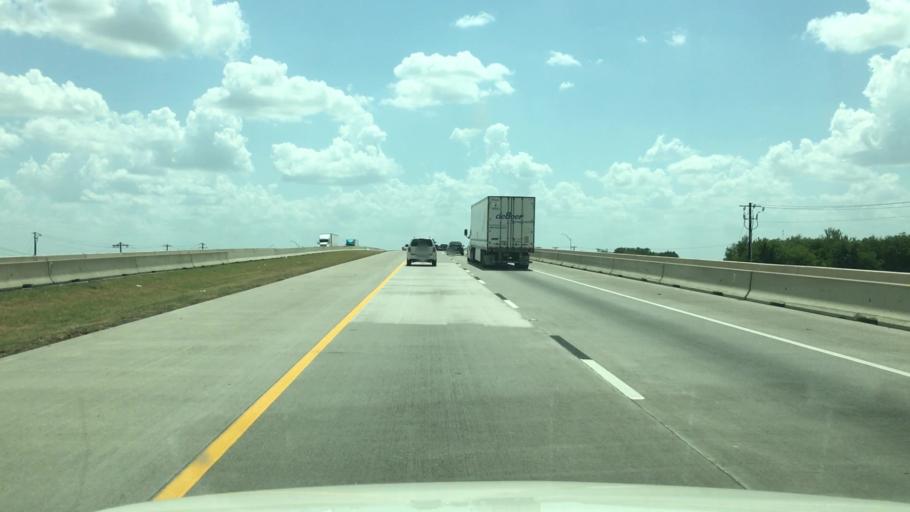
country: US
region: Texas
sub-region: Rockwall County
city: Fate
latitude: 32.9353
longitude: -96.3788
